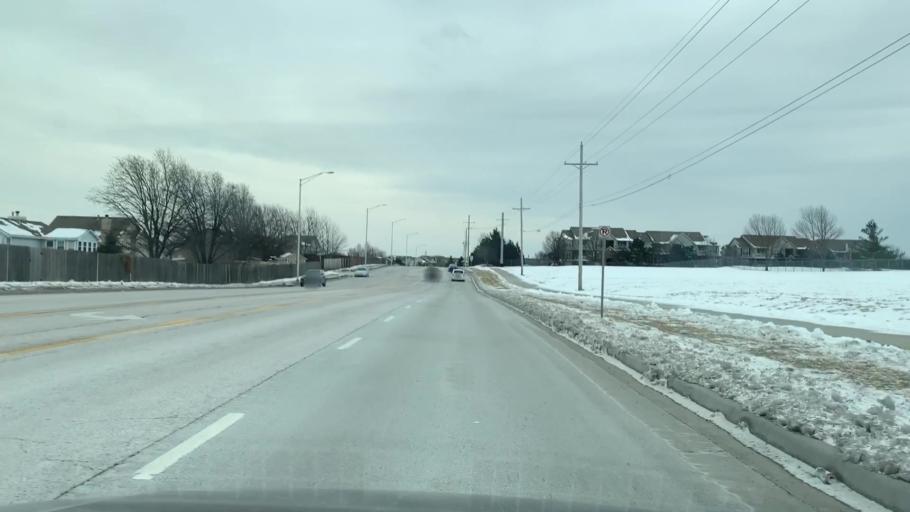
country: US
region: Missouri
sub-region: Jackson County
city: Lees Summit
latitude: 38.9304
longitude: -94.3726
